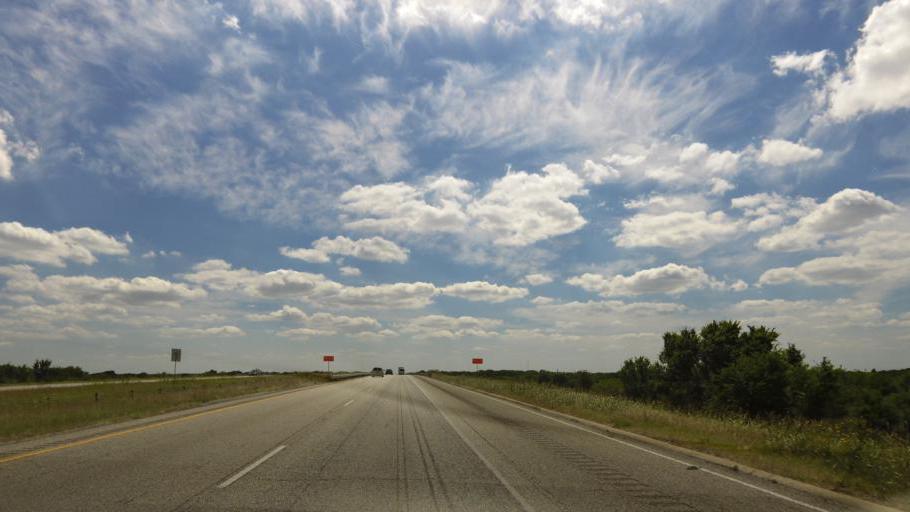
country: US
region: Texas
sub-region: Gonzales County
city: Waelder
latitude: 29.6839
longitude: -97.2665
